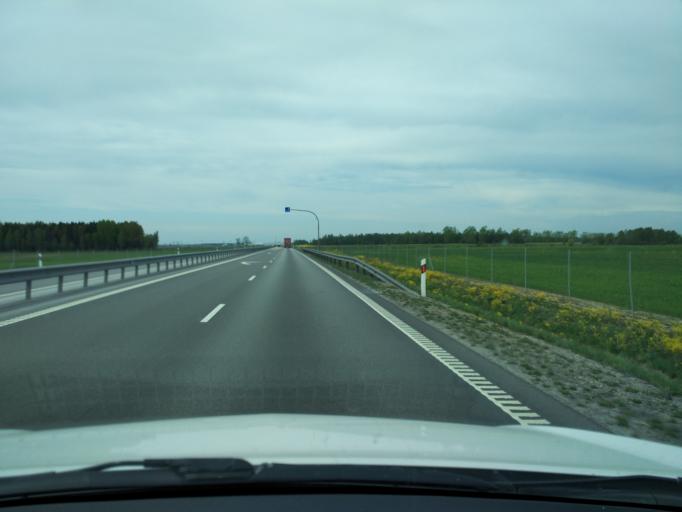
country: LT
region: Panevezys
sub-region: Panevezys City
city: Panevezys
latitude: 55.6758
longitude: 24.3246
